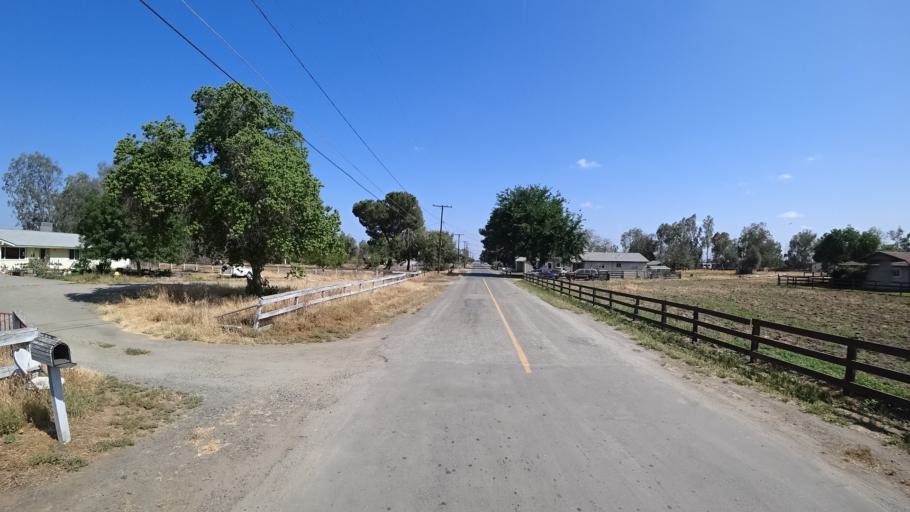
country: US
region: California
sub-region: Kings County
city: Home Garden
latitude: 36.3079
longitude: -119.6303
